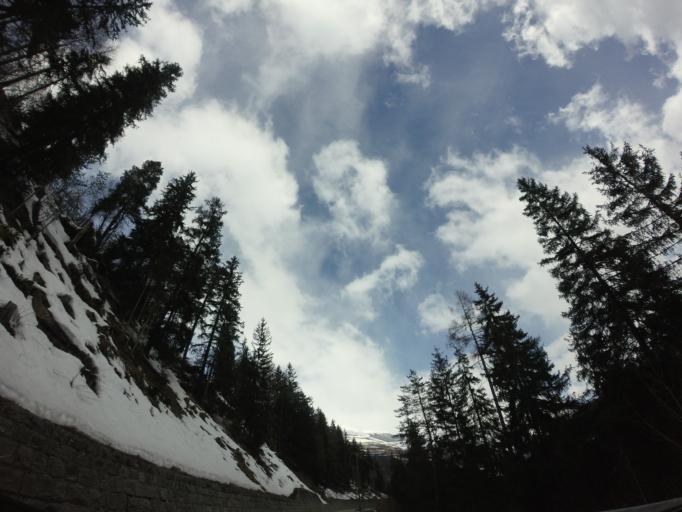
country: AT
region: Tyrol
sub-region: Politischer Bezirk Landeck
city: Nauders
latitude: 46.8507
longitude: 10.4207
